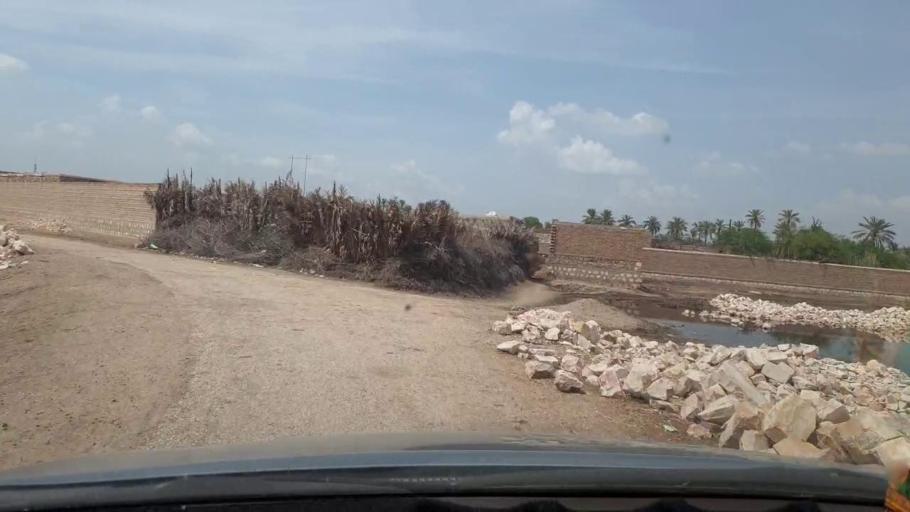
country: PK
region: Sindh
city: Khairpur
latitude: 27.4574
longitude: 68.8240
